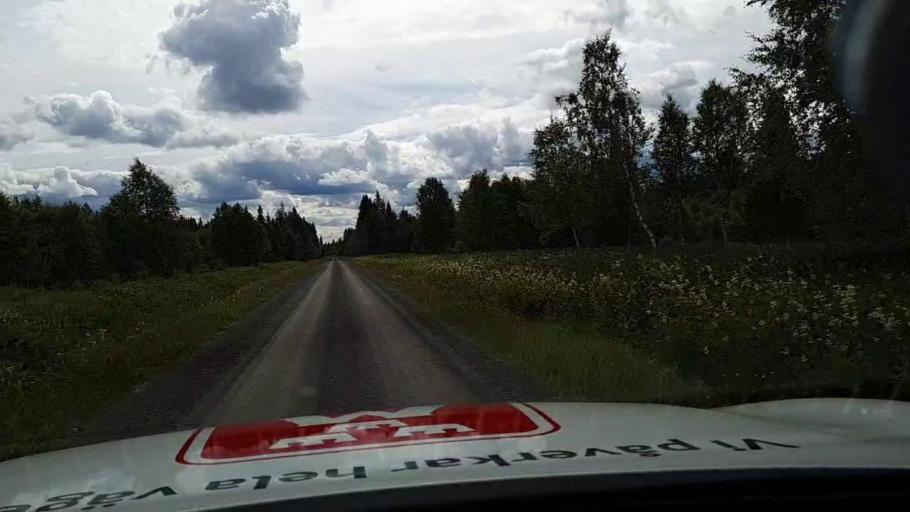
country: SE
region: Jaemtland
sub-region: OEstersunds Kommun
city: Lit
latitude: 63.2961
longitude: 15.2449
